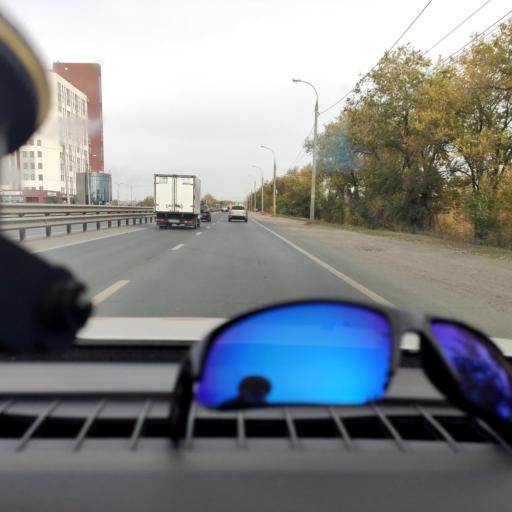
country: RU
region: Samara
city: Samara
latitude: 53.1159
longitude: 50.1660
